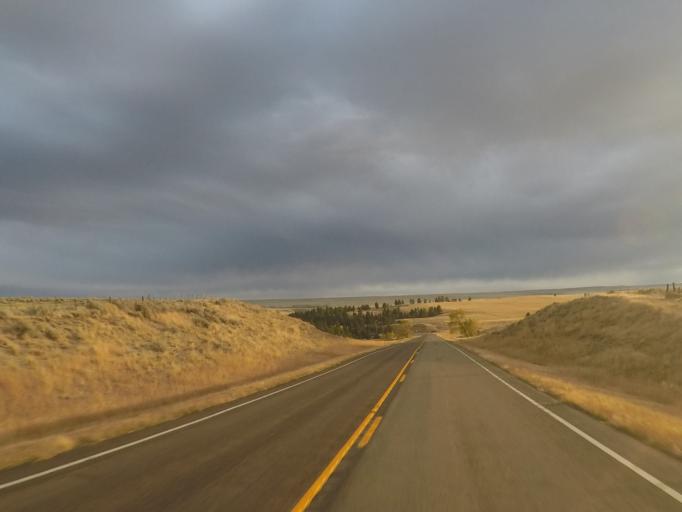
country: US
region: Montana
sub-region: Golden Valley County
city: Ryegate
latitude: 46.3107
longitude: -109.2597
